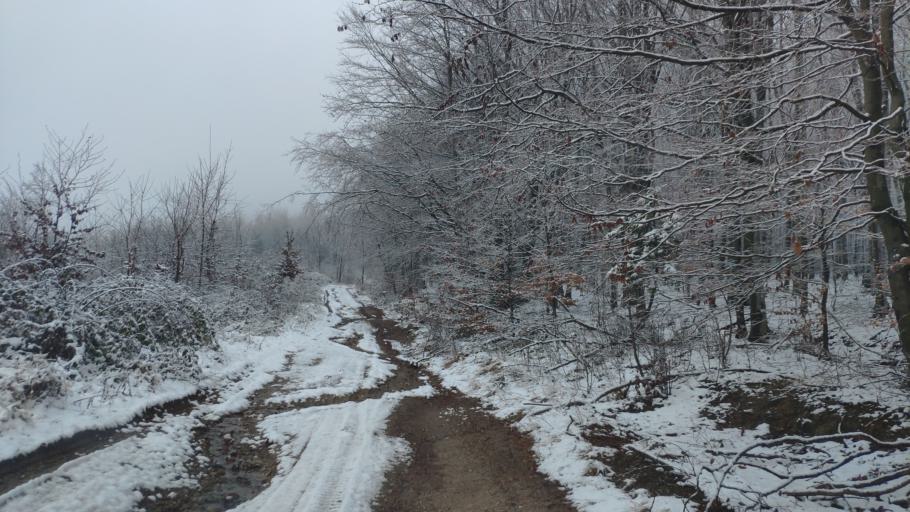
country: SK
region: Kosicky
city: Moldava nad Bodvou
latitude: 48.7425
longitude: 21.0839
